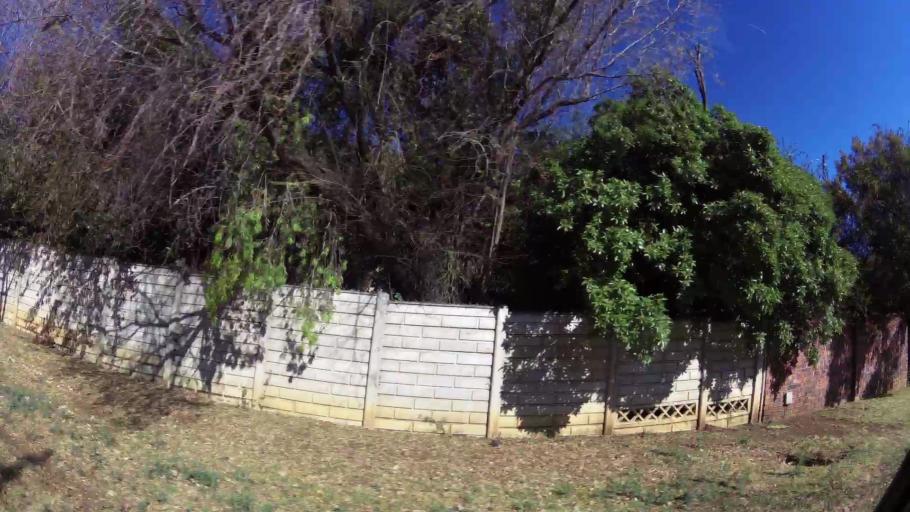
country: ZA
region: Gauteng
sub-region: City of Johannesburg Metropolitan Municipality
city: Johannesburg
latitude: -26.2776
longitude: 28.0171
